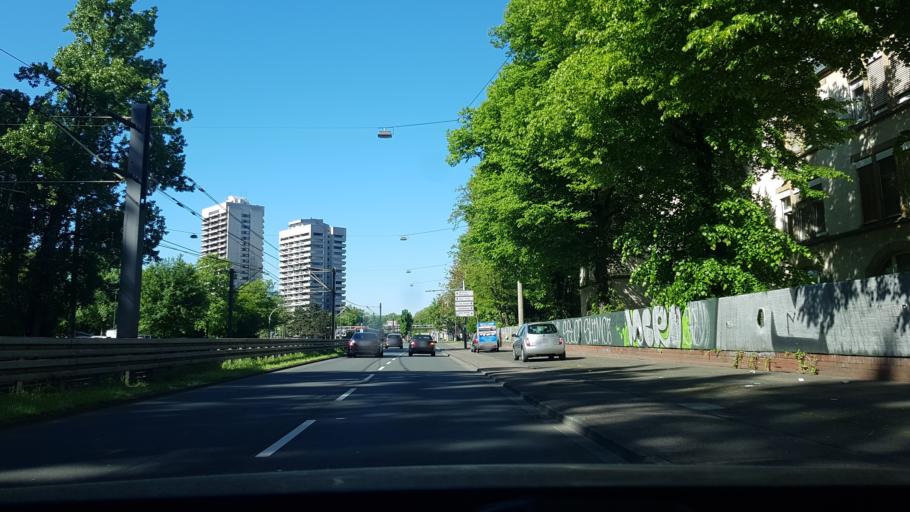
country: DE
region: North Rhine-Westphalia
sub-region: Regierungsbezirk Koln
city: Riehl
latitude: 50.9642
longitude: 6.9849
